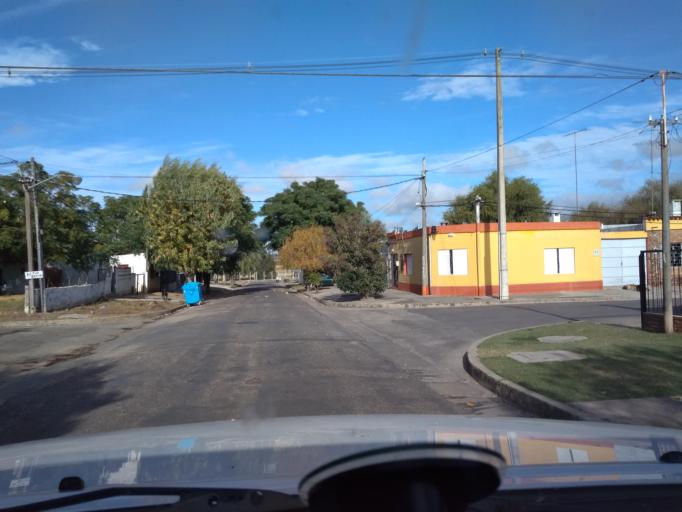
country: UY
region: Florida
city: Florida
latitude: -34.1065
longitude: -56.2145
